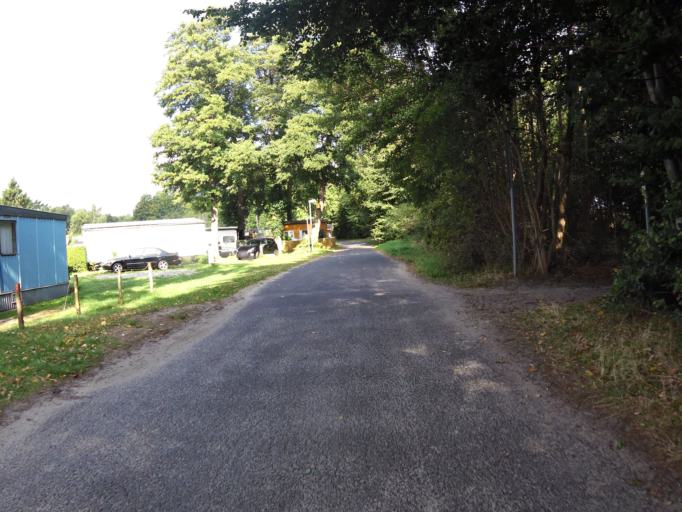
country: DE
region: Mecklenburg-Vorpommern
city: Seebad Bansin
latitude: 53.9946
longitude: 14.1095
